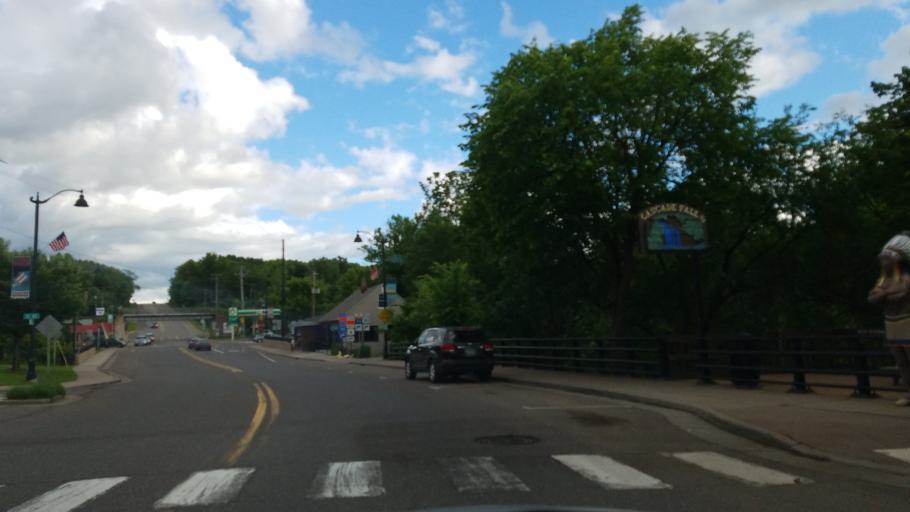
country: US
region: Wisconsin
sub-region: Polk County
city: Osceola
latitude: 45.3201
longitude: -92.7059
